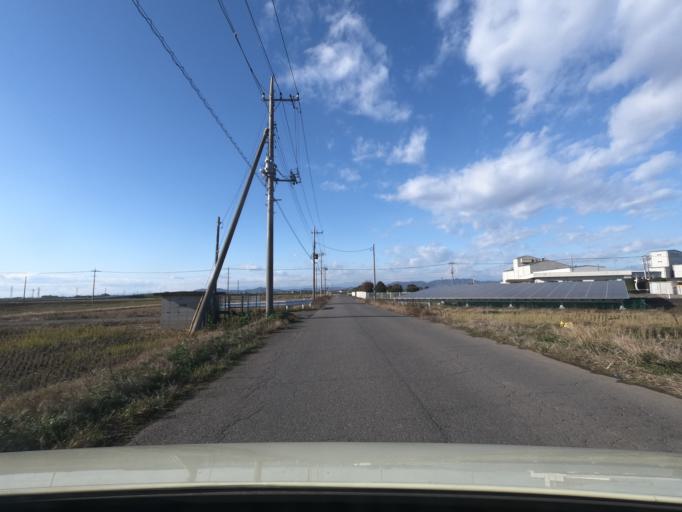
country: JP
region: Ibaraki
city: Koga
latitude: 36.2602
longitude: 139.7288
